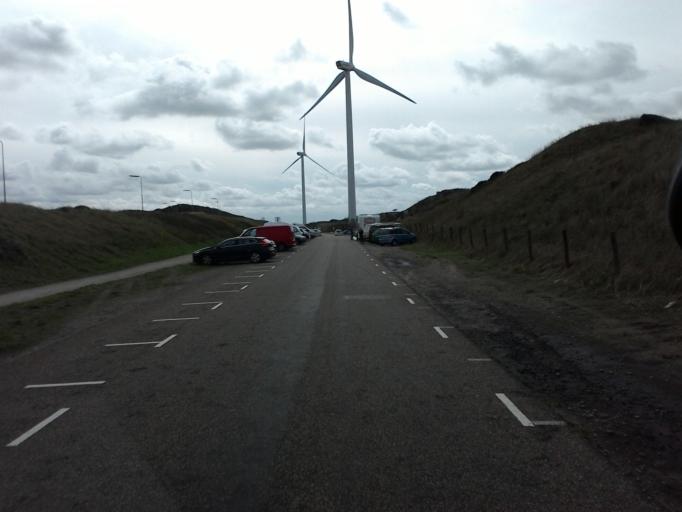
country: NL
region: North Holland
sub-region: Gemeente Velsen
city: Velsen-Zuid
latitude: 52.4753
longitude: 4.5764
